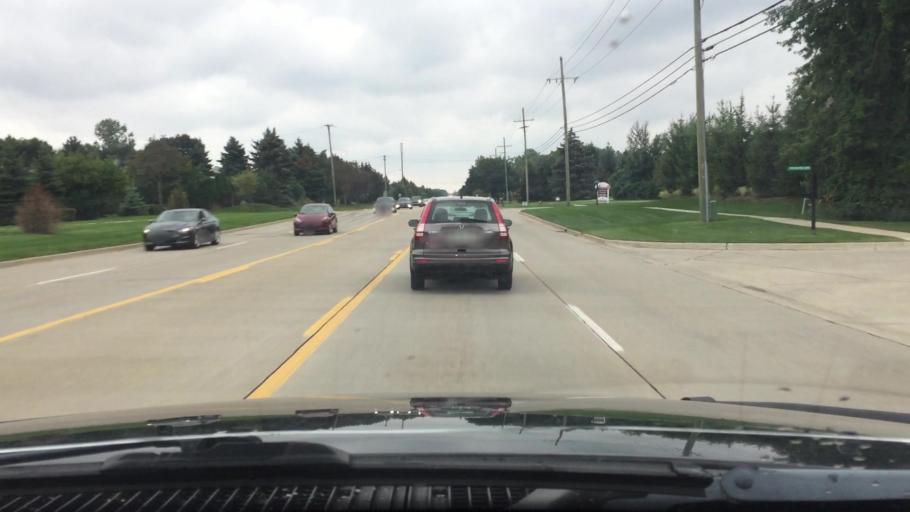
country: US
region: Michigan
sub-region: Macomb County
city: Utica
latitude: 42.6177
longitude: -83.0716
